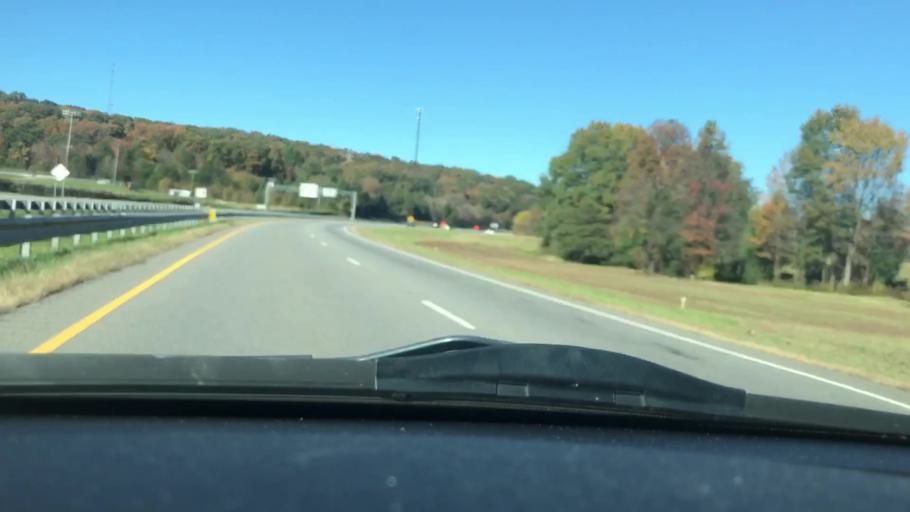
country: US
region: North Carolina
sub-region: Rockingham County
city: Mayodan
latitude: 36.4175
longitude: -79.9381
